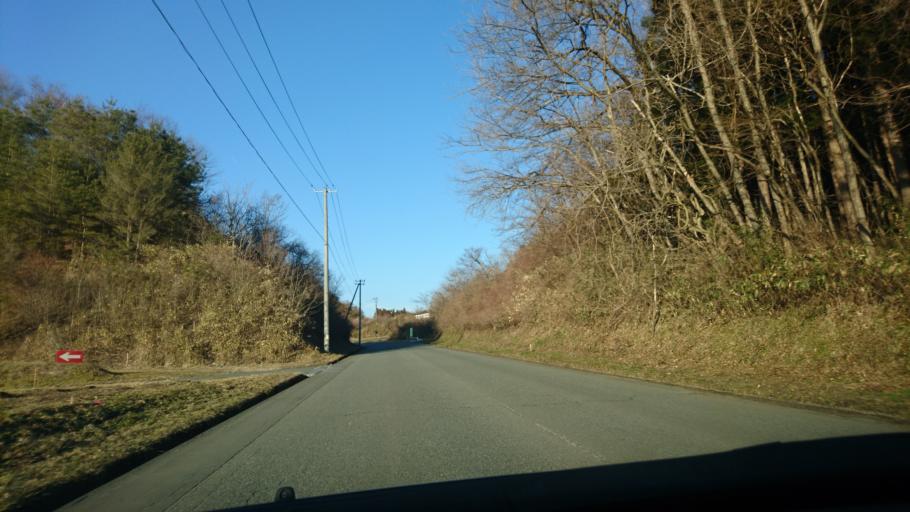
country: JP
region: Iwate
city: Ichinoseki
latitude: 38.9375
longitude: 141.3602
